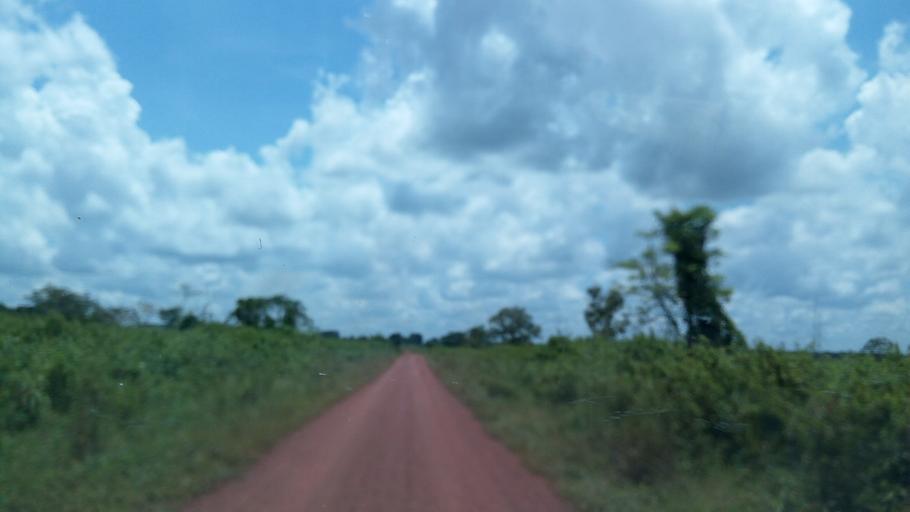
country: CD
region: Equateur
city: Libenge
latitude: 3.7734
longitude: 18.9392
